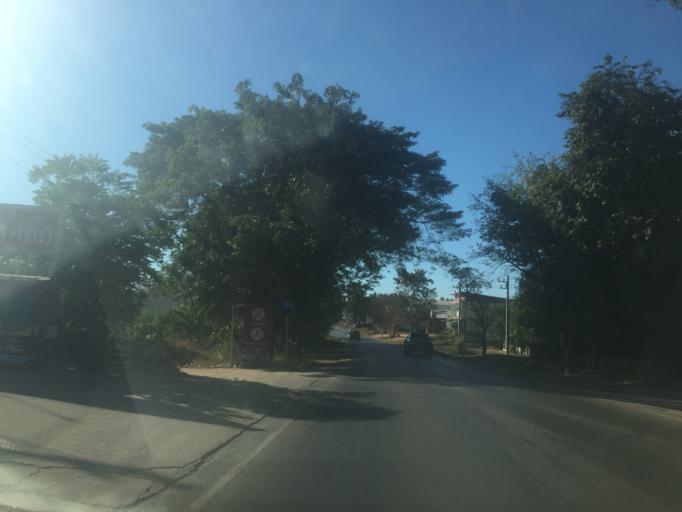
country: TH
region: Changwat Udon Thani
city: Si That
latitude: 16.9737
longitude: 103.2277
